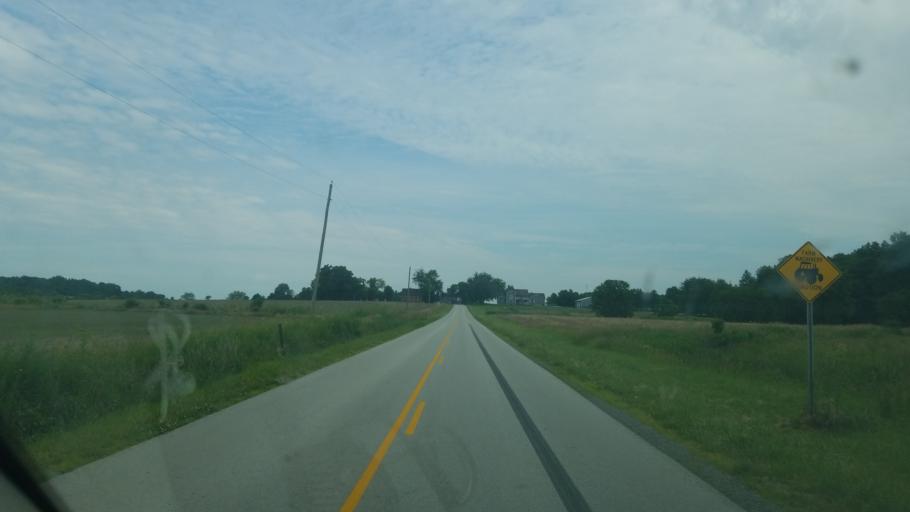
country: US
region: Ohio
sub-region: Wyandot County
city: Carey
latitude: 41.0318
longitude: -83.4398
